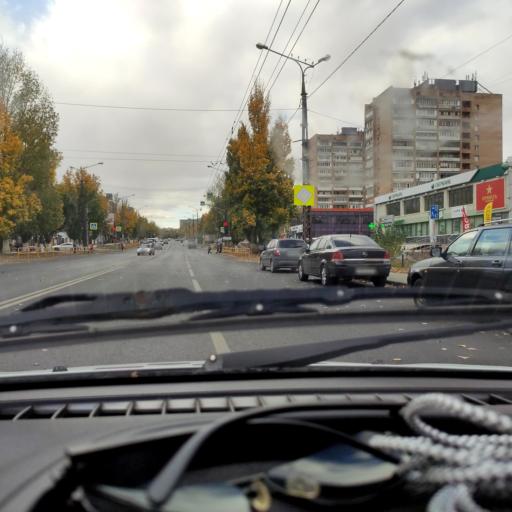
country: RU
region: Samara
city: Zhigulevsk
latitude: 53.4815
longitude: 49.4811
